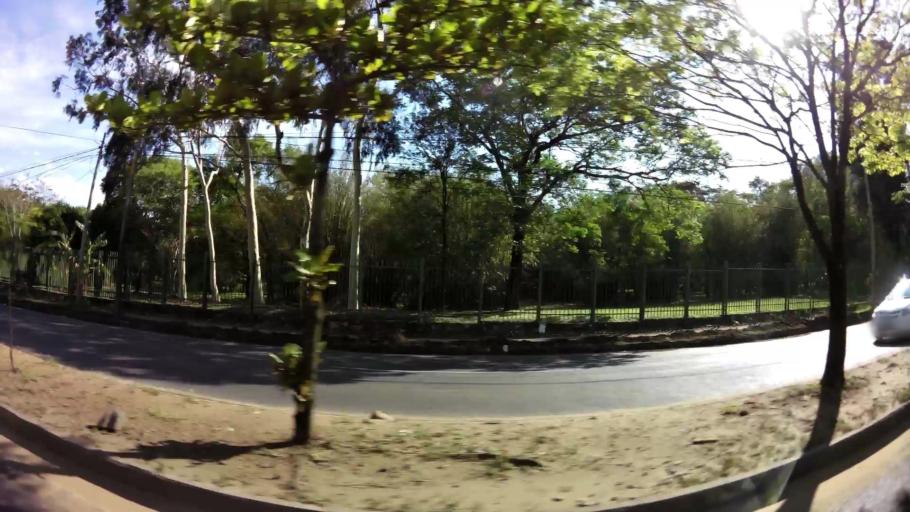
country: PY
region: Asuncion
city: Asuncion
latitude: -25.2550
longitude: -57.5729
